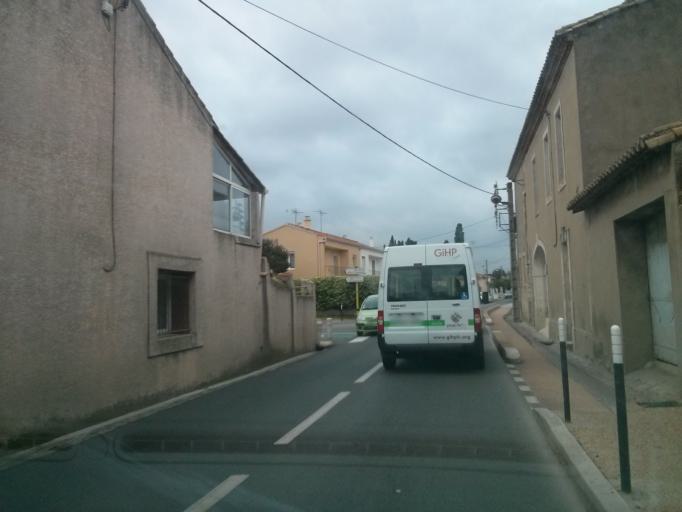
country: FR
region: Languedoc-Roussillon
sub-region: Departement de l'Herault
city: Lunel
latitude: 43.6742
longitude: 4.1279
